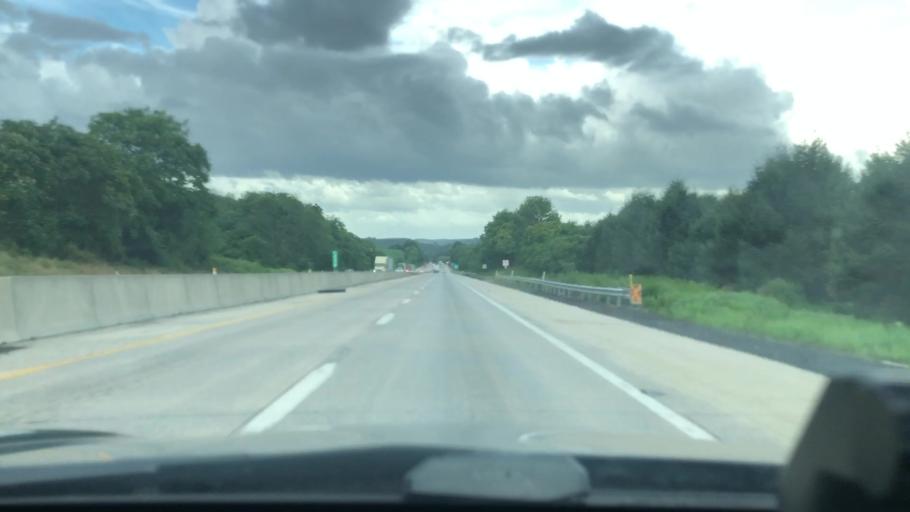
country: US
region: Pennsylvania
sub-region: Berks County
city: Hamburg
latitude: 40.5747
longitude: -75.9268
